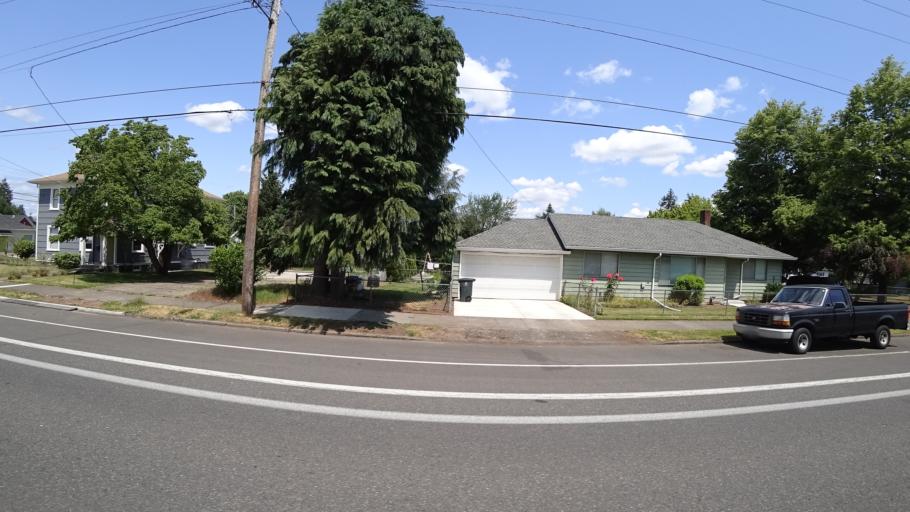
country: US
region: Oregon
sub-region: Washington County
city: West Haven
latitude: 45.5924
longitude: -122.7430
